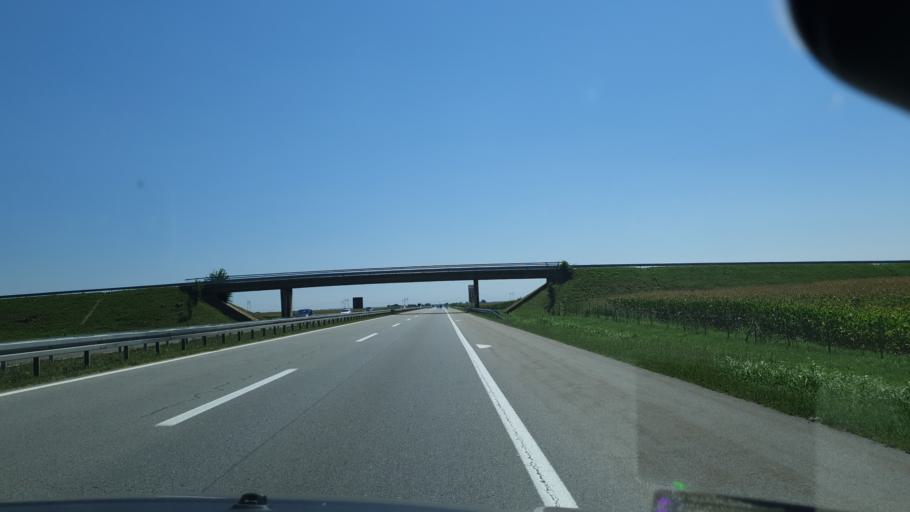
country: RS
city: Krcedin
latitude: 45.0891
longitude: 20.1271
